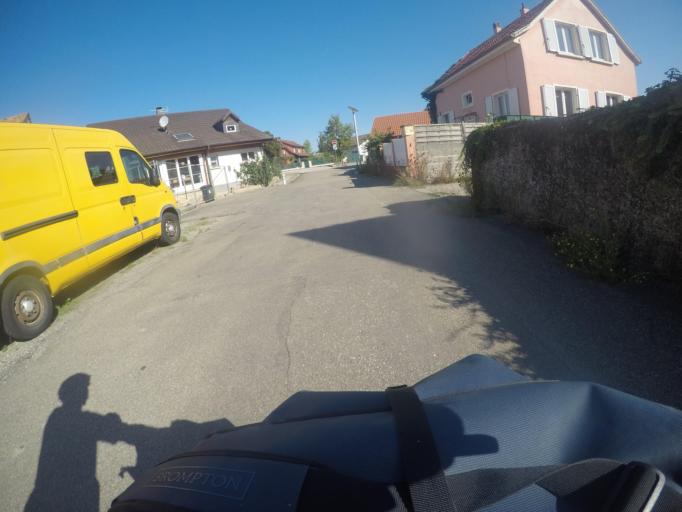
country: FR
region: Alsace
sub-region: Departement du Haut-Rhin
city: Ottmarsheim
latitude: 47.7848
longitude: 7.5056
